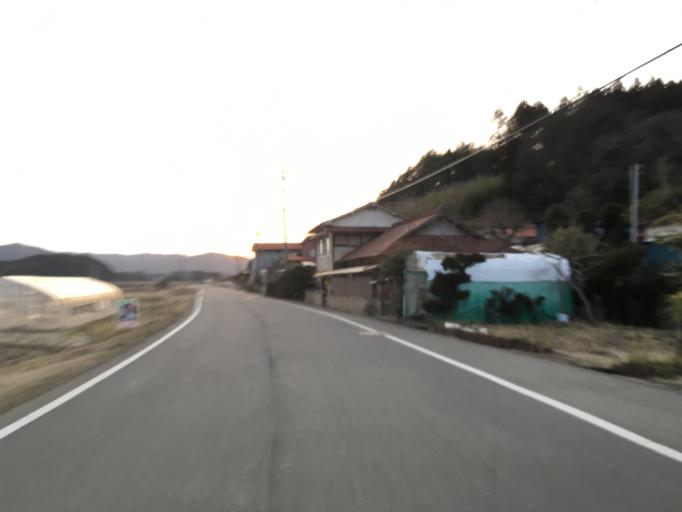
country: JP
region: Fukushima
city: Ishikawa
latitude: 37.0663
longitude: 140.3208
